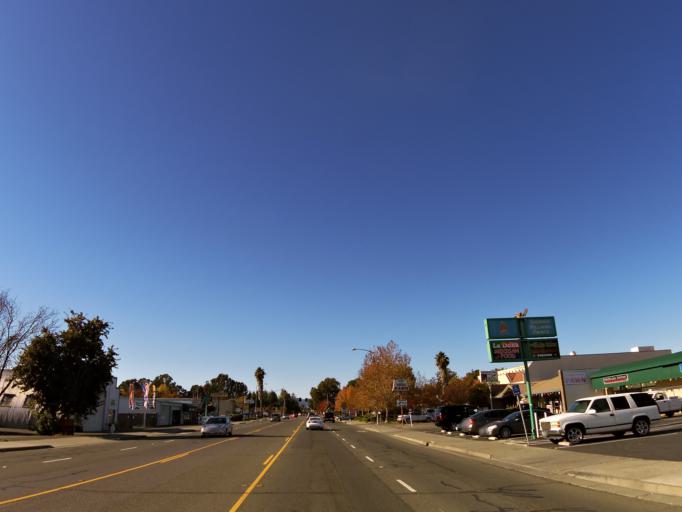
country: US
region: California
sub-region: Solano County
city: Fairfield
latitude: 38.2493
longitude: -122.0539
